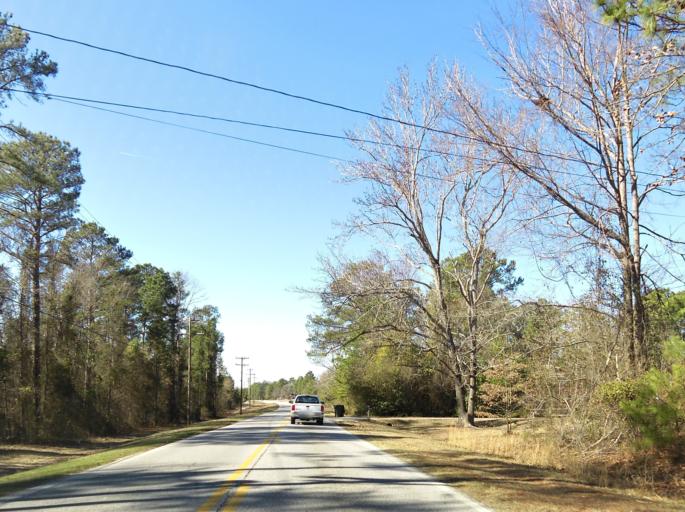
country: US
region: Georgia
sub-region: Bibb County
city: West Point
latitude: 32.7567
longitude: -83.7532
